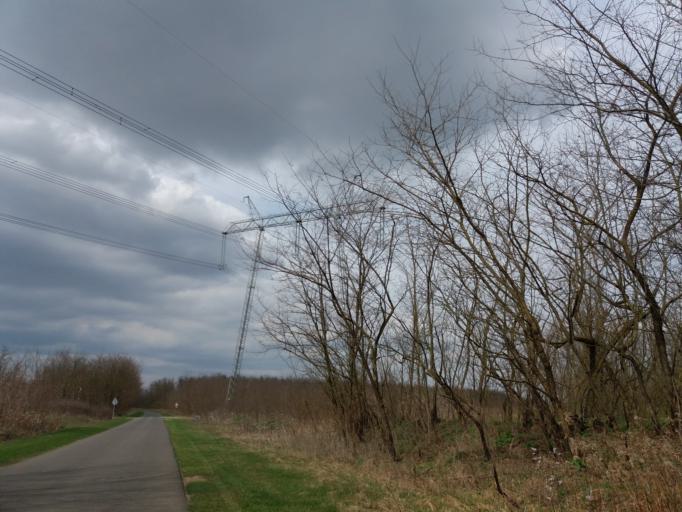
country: HU
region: Szabolcs-Szatmar-Bereg
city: Petnehaza
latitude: 48.0761
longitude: 22.0435
